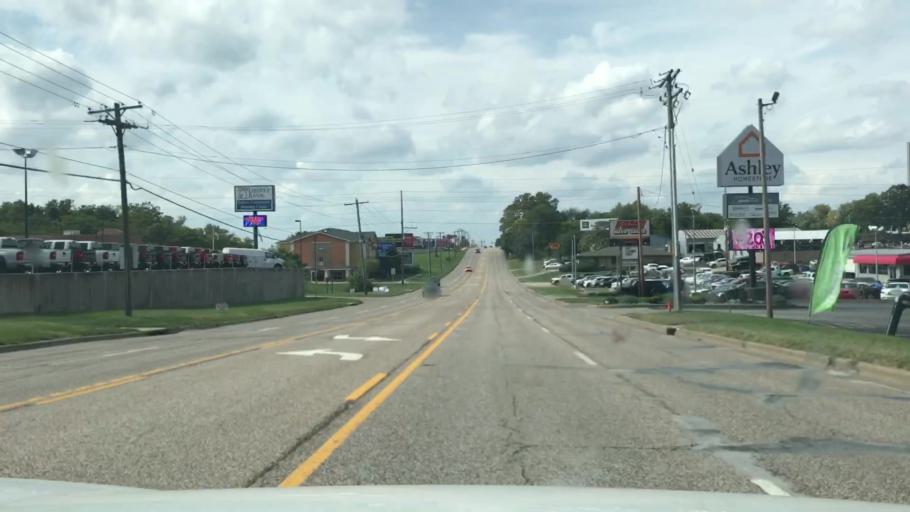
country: US
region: Illinois
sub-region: Adams County
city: Quincy
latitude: 39.9351
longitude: -91.3470
